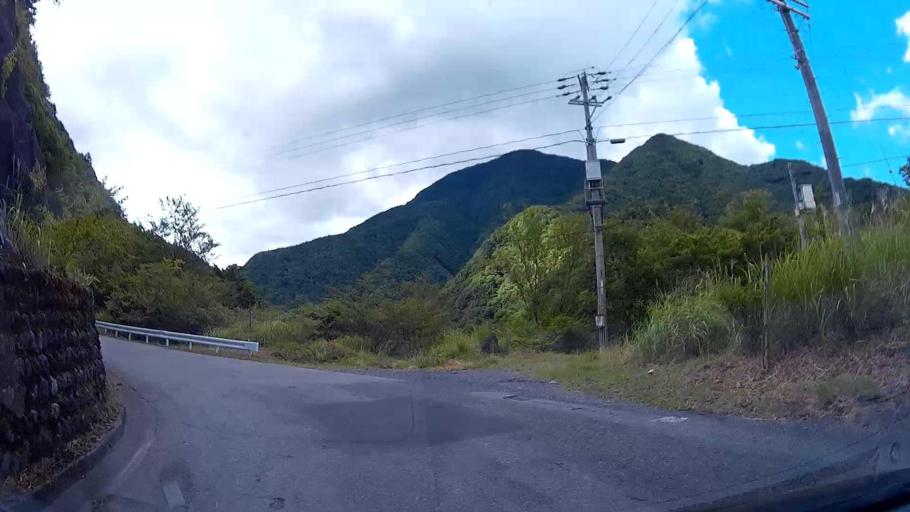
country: JP
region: Shizuoka
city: Shizuoka-shi
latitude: 35.3025
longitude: 138.2066
